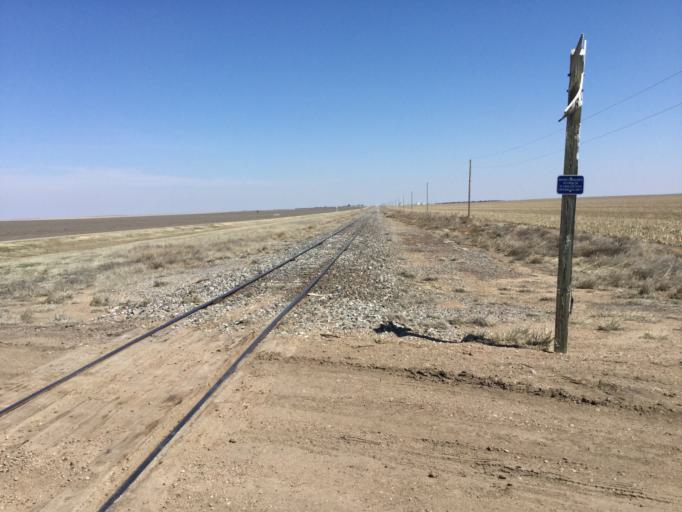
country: US
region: Kansas
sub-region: Stanton County
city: Johnson
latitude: 37.5389
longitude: -101.8345
